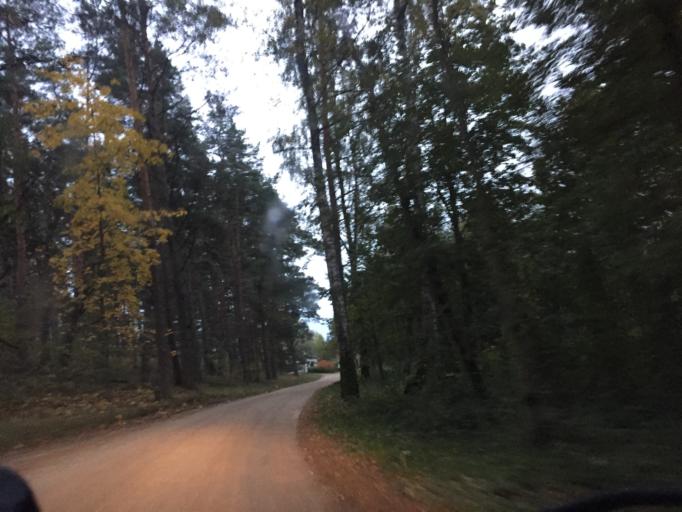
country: LV
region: Adazi
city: Adazi
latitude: 57.0854
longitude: 24.3495
